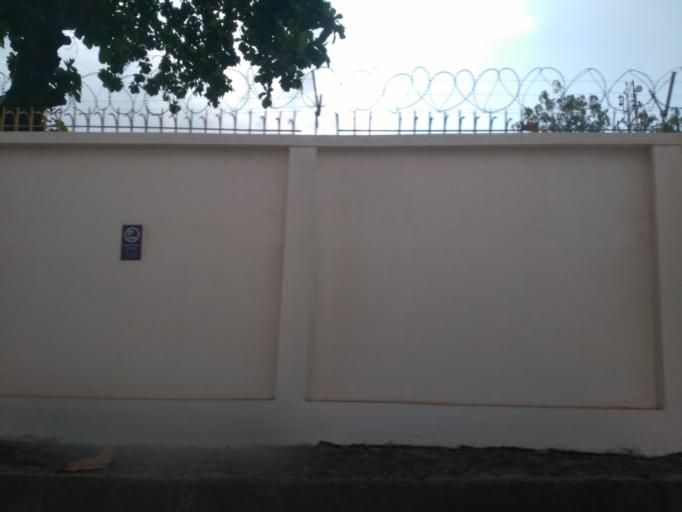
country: TZ
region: Dar es Salaam
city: Dar es Salaam
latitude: -6.7995
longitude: 39.2765
